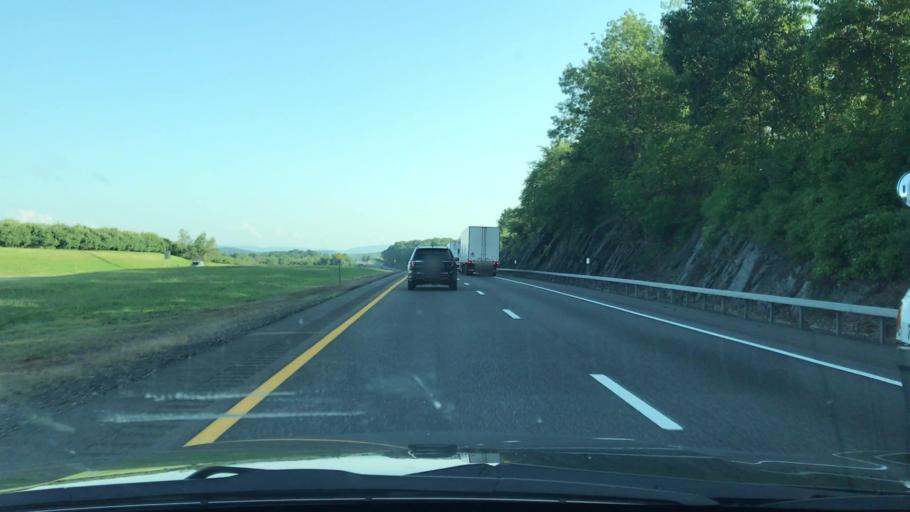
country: US
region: New York
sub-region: Ulster County
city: Plattekill
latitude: 41.6429
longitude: -74.0775
